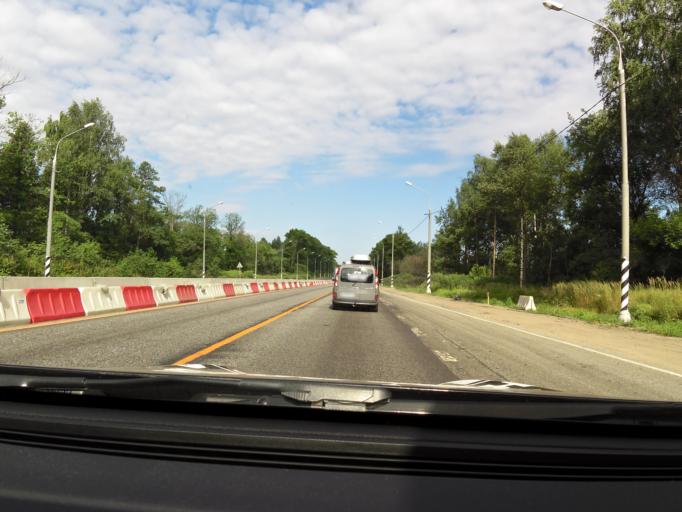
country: RU
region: Tverskaya
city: Emmaus
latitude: 56.7561
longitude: 36.1896
